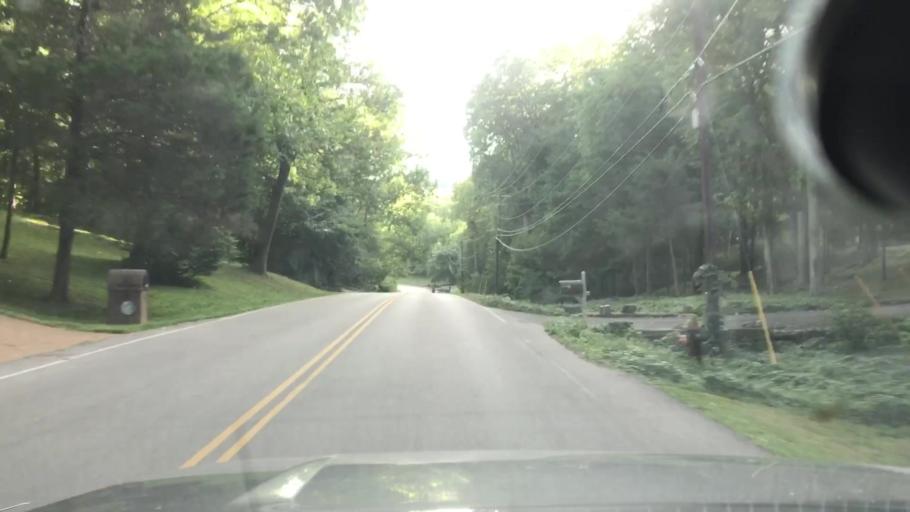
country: US
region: Tennessee
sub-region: Davidson County
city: Forest Hills
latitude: 36.0478
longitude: -86.8405
